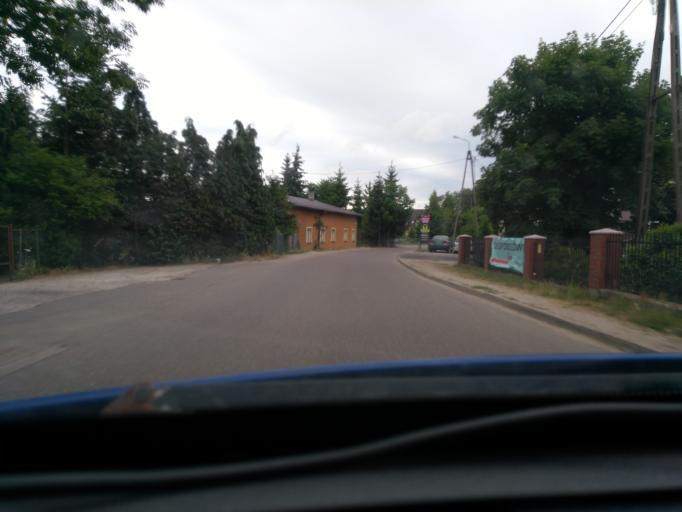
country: PL
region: Pomeranian Voivodeship
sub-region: Powiat kartuski
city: Banino
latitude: 54.3935
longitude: 18.4064
